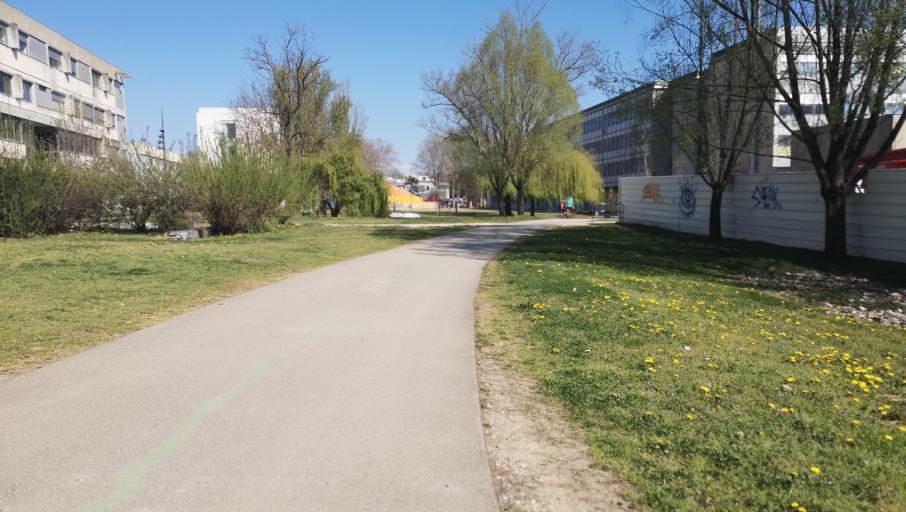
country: FR
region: Rhone-Alpes
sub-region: Departement du Rhone
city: Villeurbanne
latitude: 45.7832
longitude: 4.8739
